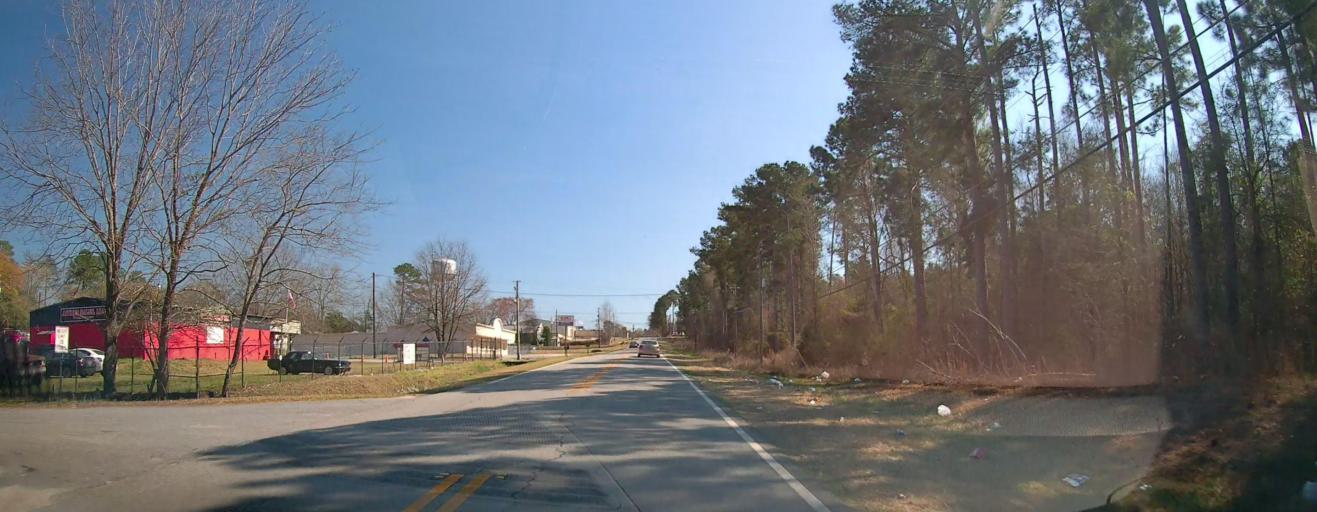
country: US
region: Georgia
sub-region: Bibb County
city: Macon
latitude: 32.8759
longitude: -83.5636
